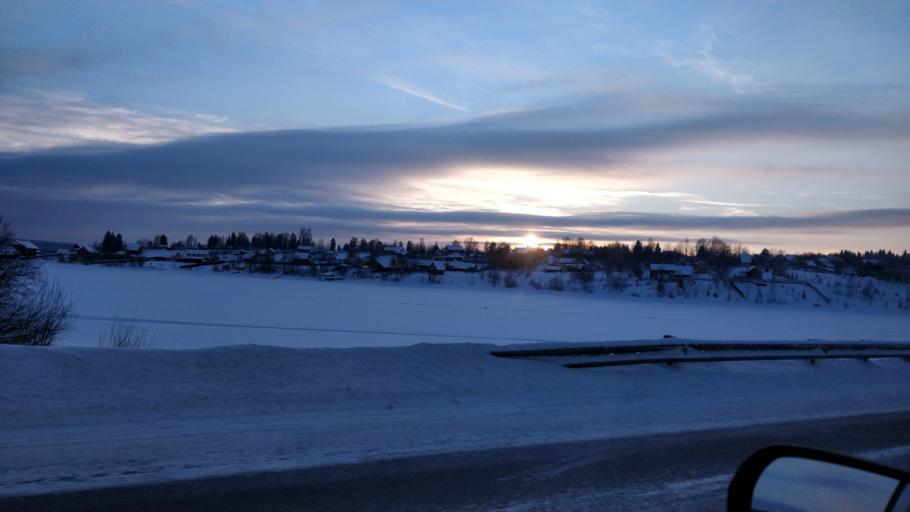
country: RU
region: Perm
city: Sylva
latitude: 58.2963
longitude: 56.8580
